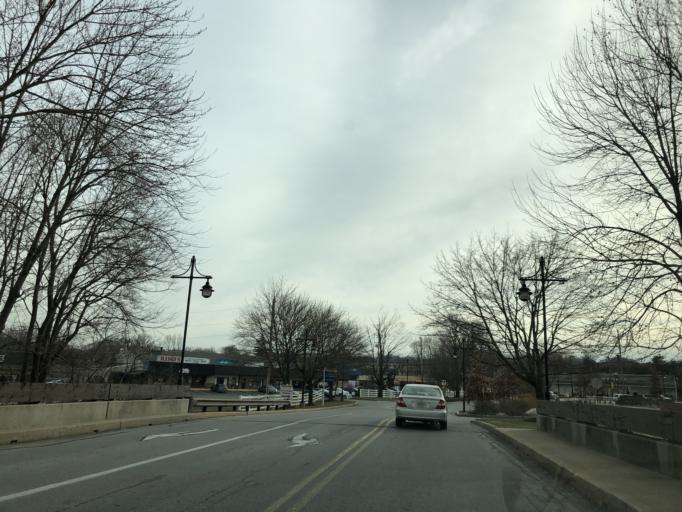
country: US
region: Pennsylvania
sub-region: Chester County
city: Exton
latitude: 40.0299
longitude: -75.6224
